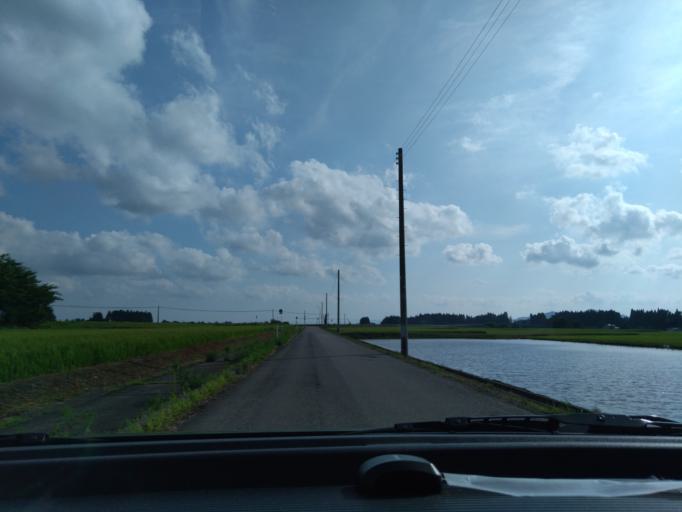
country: JP
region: Akita
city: Kakunodatemachi
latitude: 39.5872
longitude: 140.6071
